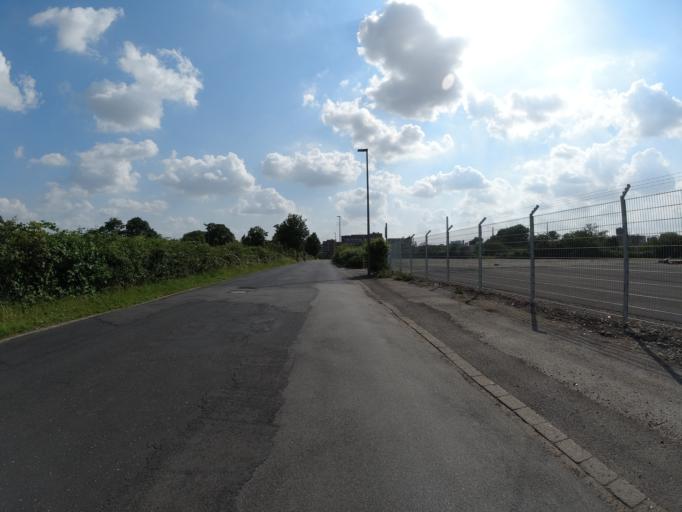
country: DE
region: North Rhine-Westphalia
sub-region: Regierungsbezirk Dusseldorf
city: Moers
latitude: 51.3735
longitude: 6.6674
